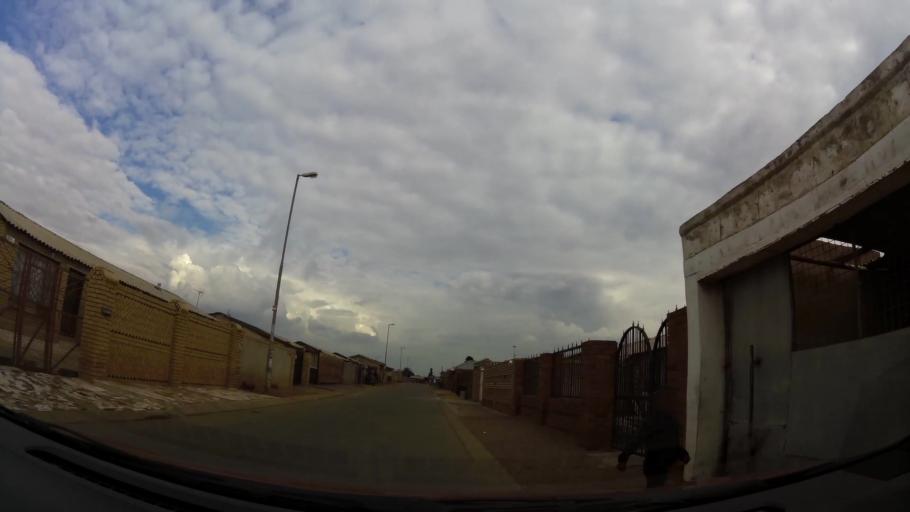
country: ZA
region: Gauteng
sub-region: City of Johannesburg Metropolitan Municipality
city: Soweto
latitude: -26.2468
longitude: 27.8452
